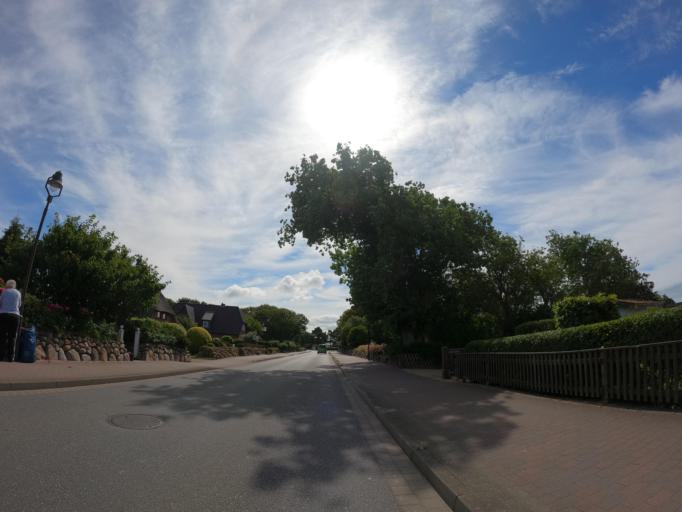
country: DE
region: Schleswig-Holstein
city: Tinnum
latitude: 54.9008
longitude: 8.3211
